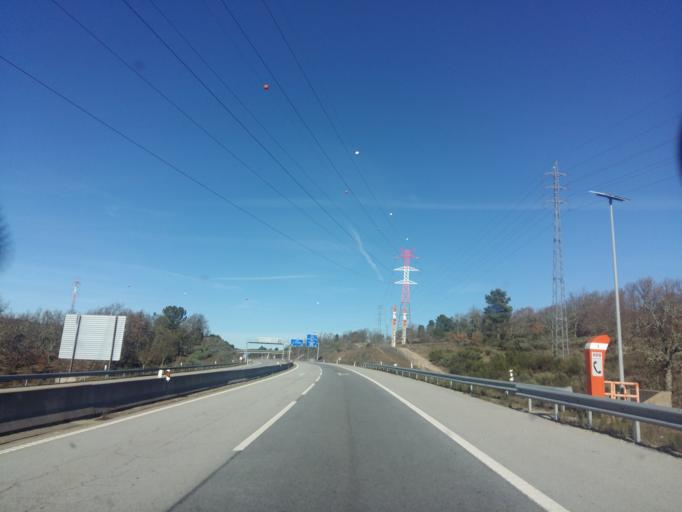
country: PT
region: Guarda
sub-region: Guarda
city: Sequeira
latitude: 40.5562
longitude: -7.2167
